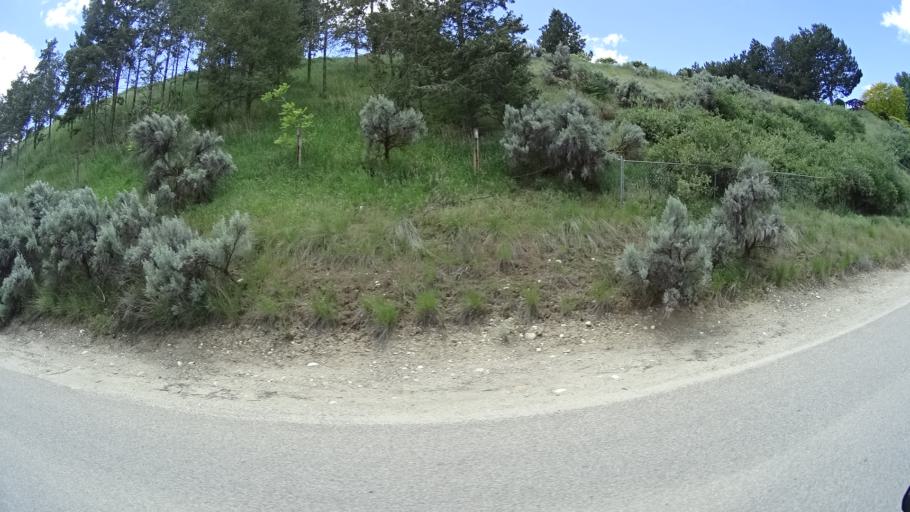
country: US
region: Idaho
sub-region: Ada County
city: Eagle
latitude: 43.6639
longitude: -116.3315
